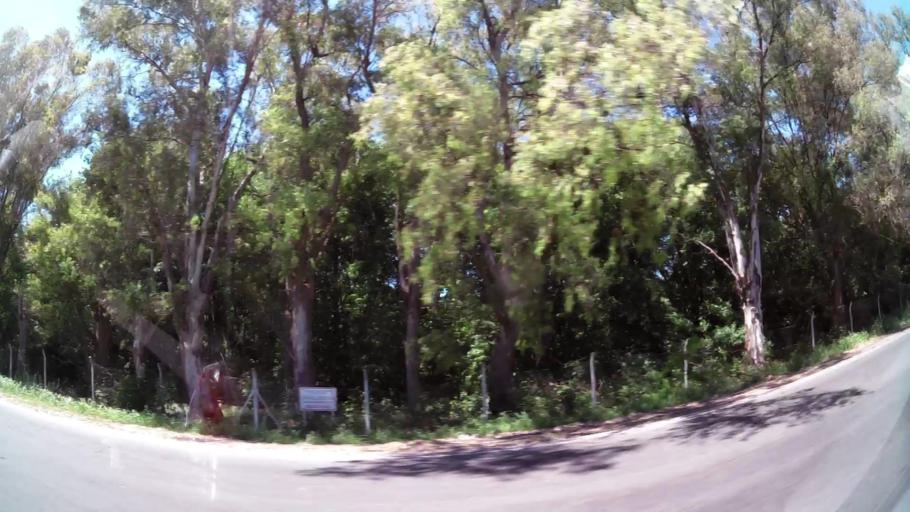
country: AR
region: Buenos Aires
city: Hurlingham
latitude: -34.5200
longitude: -58.6740
